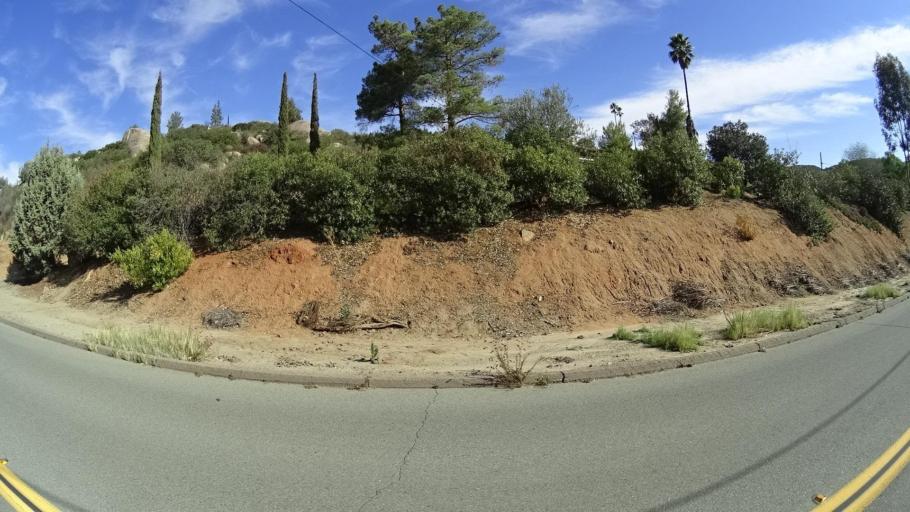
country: US
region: California
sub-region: San Diego County
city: Alpine
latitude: 32.8180
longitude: -116.7462
